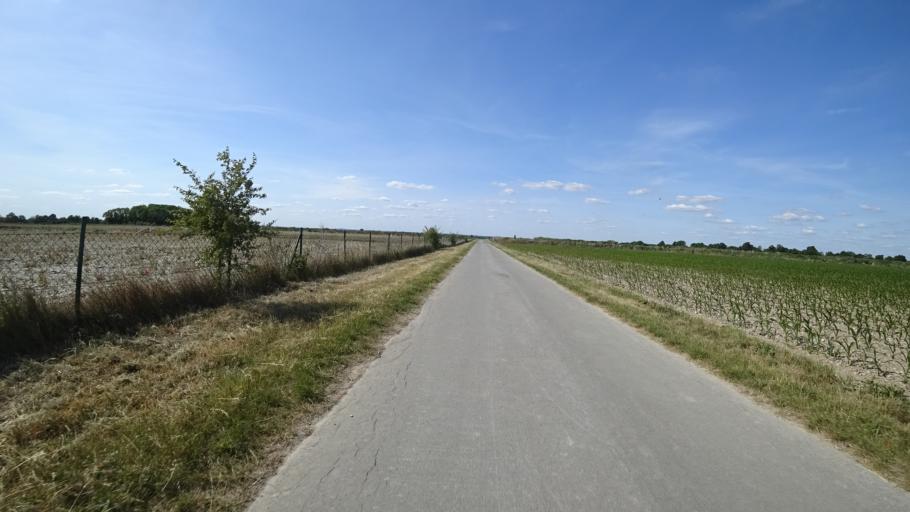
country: DE
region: North Rhine-Westphalia
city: Erwitte
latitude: 51.6071
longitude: 8.3767
